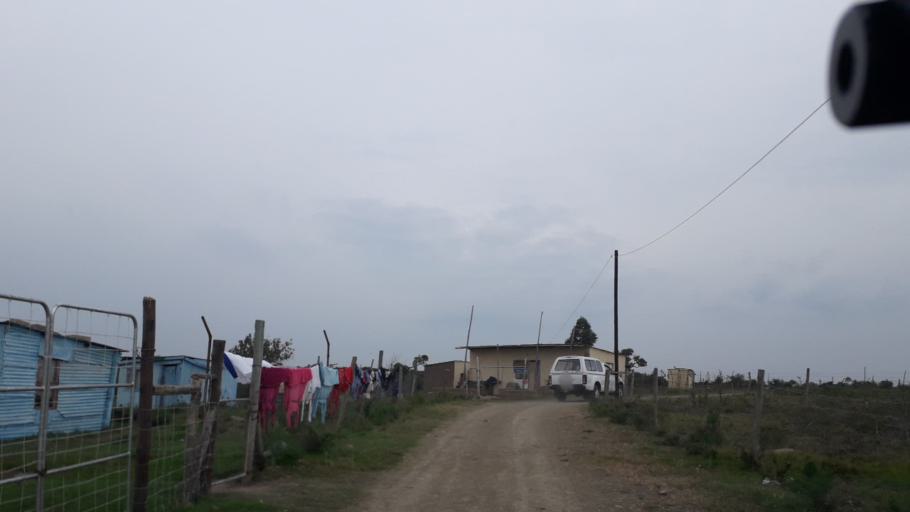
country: ZA
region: Eastern Cape
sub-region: Buffalo City Metropolitan Municipality
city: Bhisho
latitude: -32.8373
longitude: 27.3683
